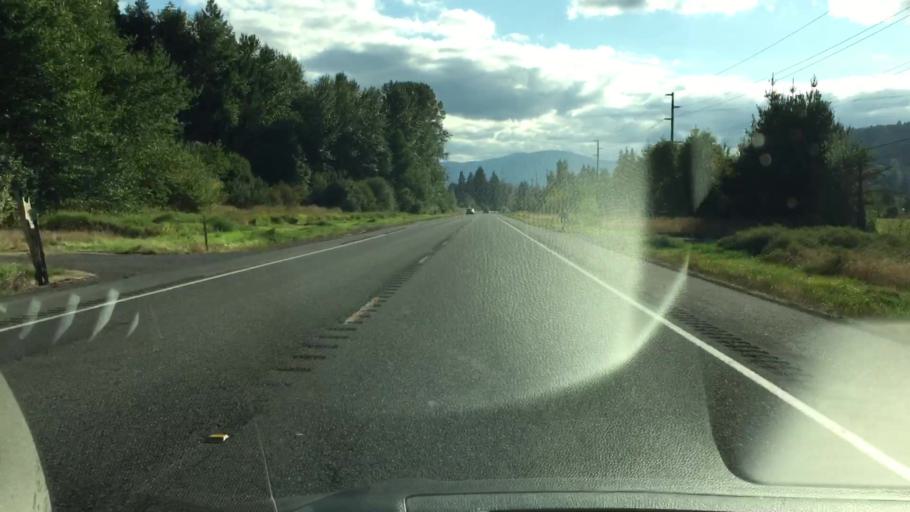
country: US
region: Washington
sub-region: Lewis County
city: Morton
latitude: 46.5231
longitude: -122.1475
